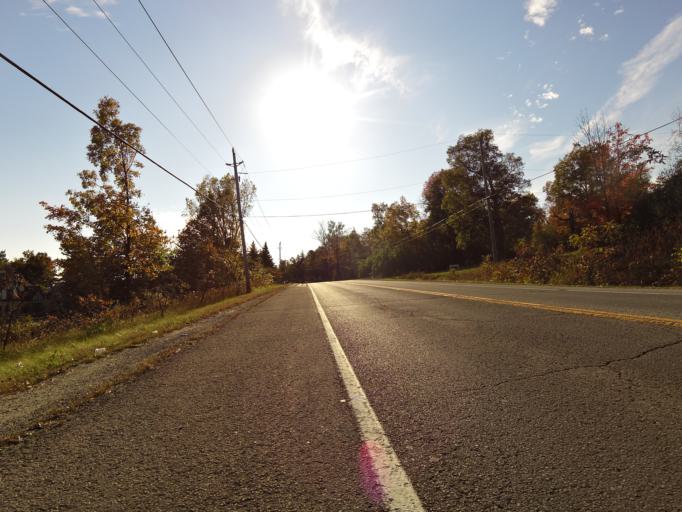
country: CA
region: Ontario
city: Kingston
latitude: 44.2349
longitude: -76.6223
